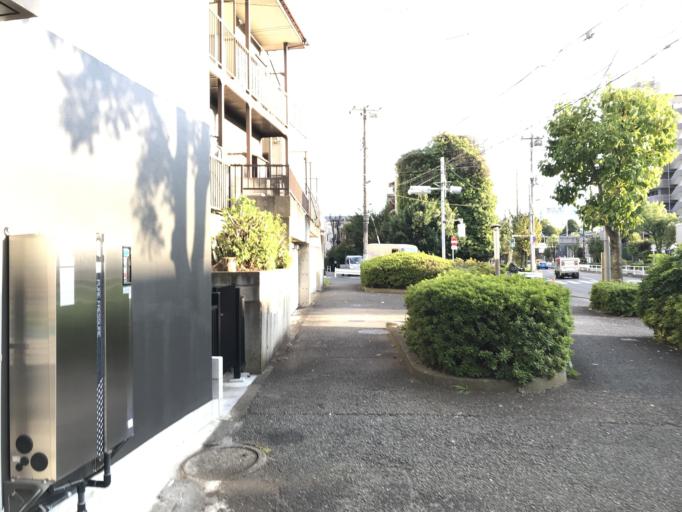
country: JP
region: Kanagawa
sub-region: Kawasaki-shi
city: Kawasaki
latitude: 35.5761
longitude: 139.6839
